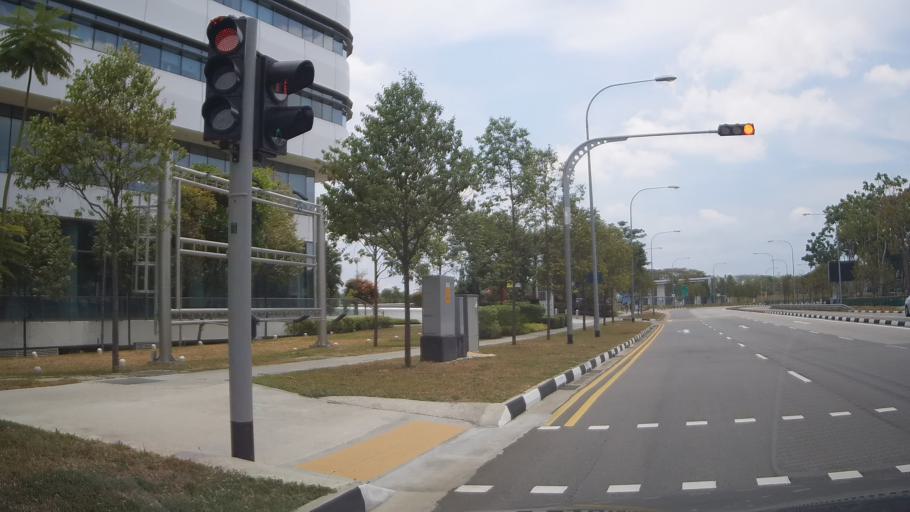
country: SG
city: Singapore
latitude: 1.3397
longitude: 103.9626
